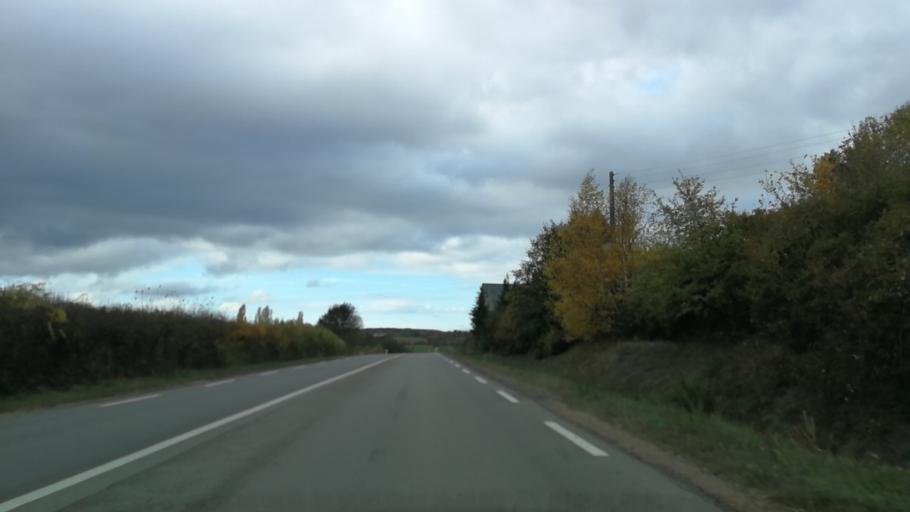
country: FR
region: Bourgogne
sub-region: Departement de la Cote-d'Or
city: Saulieu
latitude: 47.2680
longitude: 4.2568
